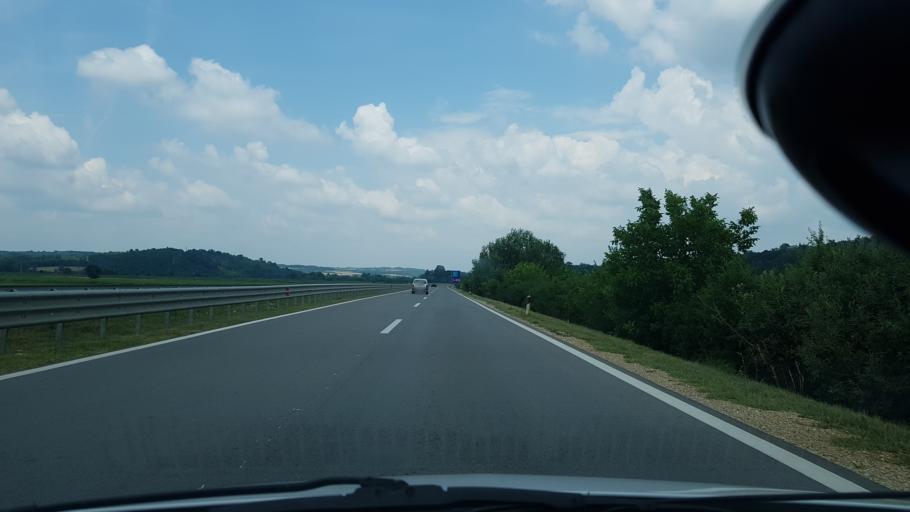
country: RS
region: Central Serbia
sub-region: Sumadijski Okrug
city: Batocina
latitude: 44.1302
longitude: 21.0192
